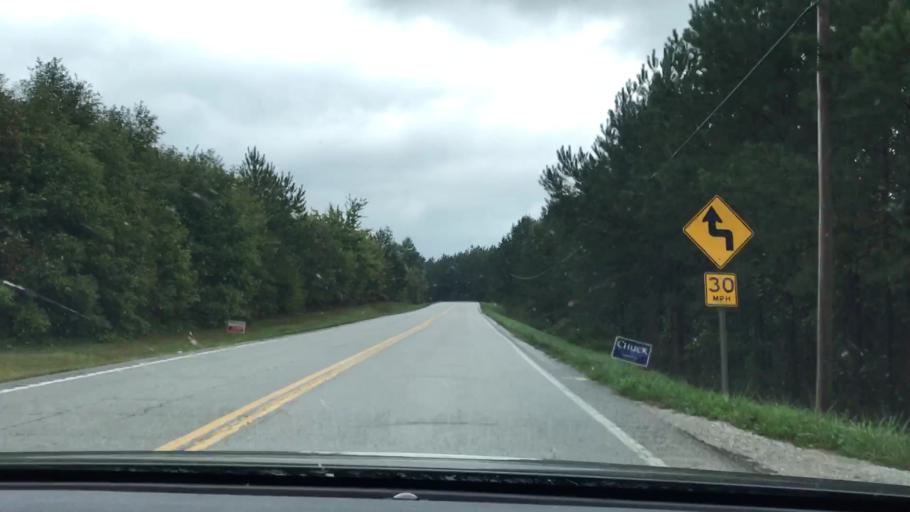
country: US
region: Tennessee
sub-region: Scott County
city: Huntsville
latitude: 36.3362
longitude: -84.6358
